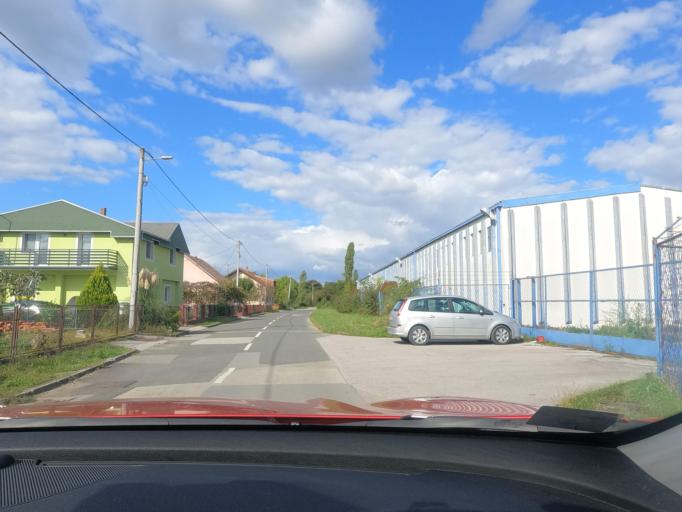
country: HR
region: Sisacko-Moslavacka
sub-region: Grad Sisak
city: Sisak
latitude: 45.4996
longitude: 16.3521
